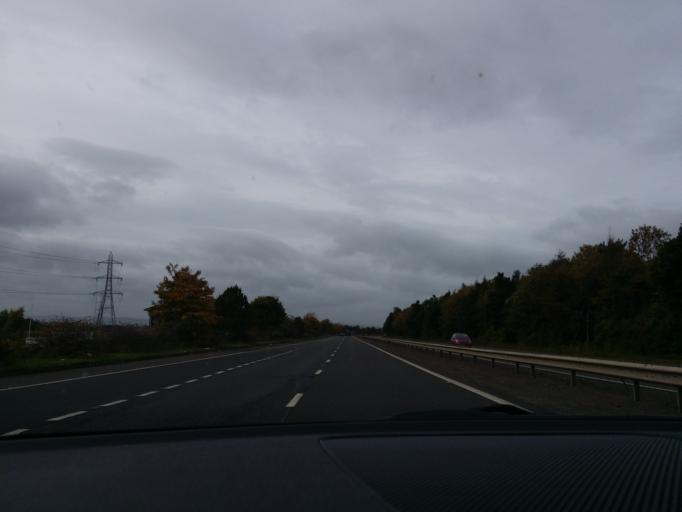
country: GB
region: Scotland
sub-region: Falkirk
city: Grangemouth
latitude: 55.9990
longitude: -3.7237
